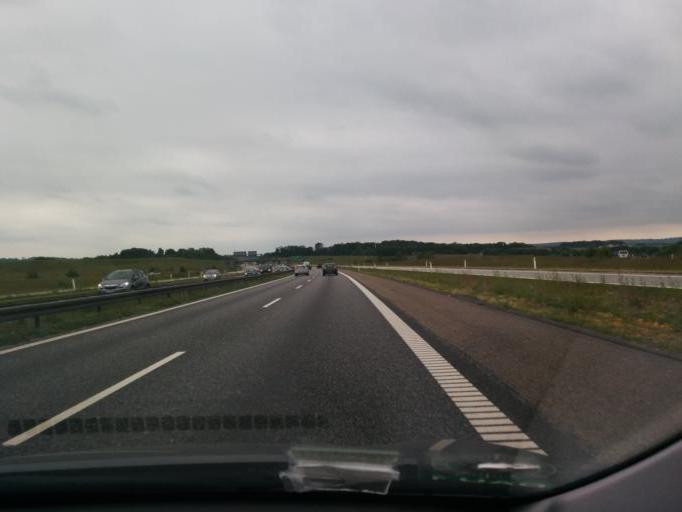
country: DK
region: Central Jutland
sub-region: Arhus Kommune
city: Framlev
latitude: 56.1604
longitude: 10.0459
